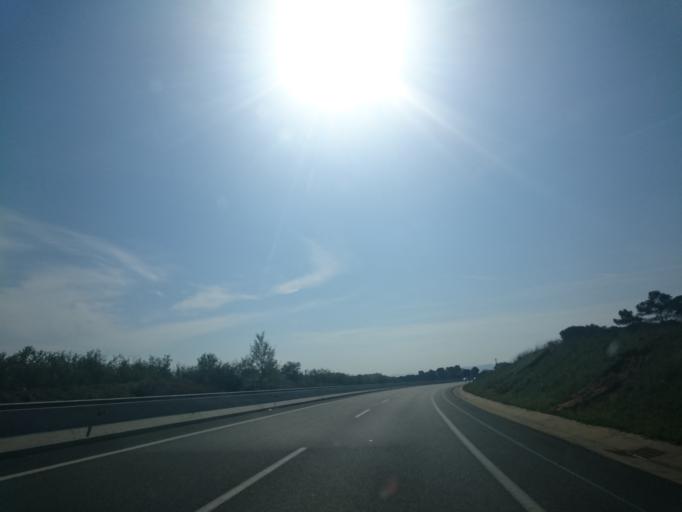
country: ES
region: Catalonia
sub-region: Provincia de Girona
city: Brunyola
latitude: 41.8823
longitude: 2.6855
